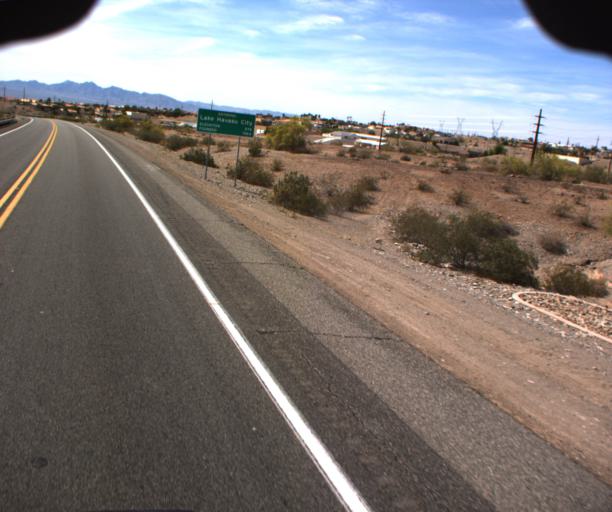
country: US
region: Arizona
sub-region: Mohave County
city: Lake Havasu City
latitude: 34.4500
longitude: -114.2453
